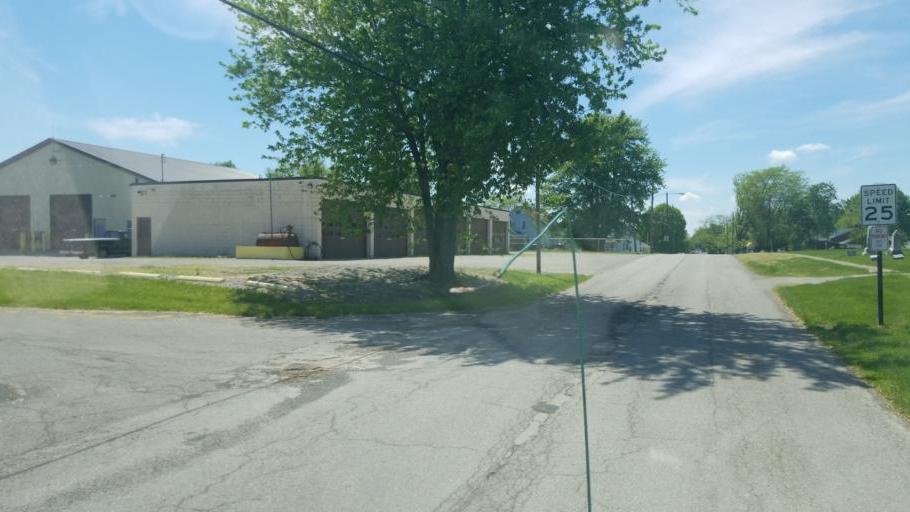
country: US
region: Ohio
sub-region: Huron County
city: Willard
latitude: 41.0664
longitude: -82.8813
